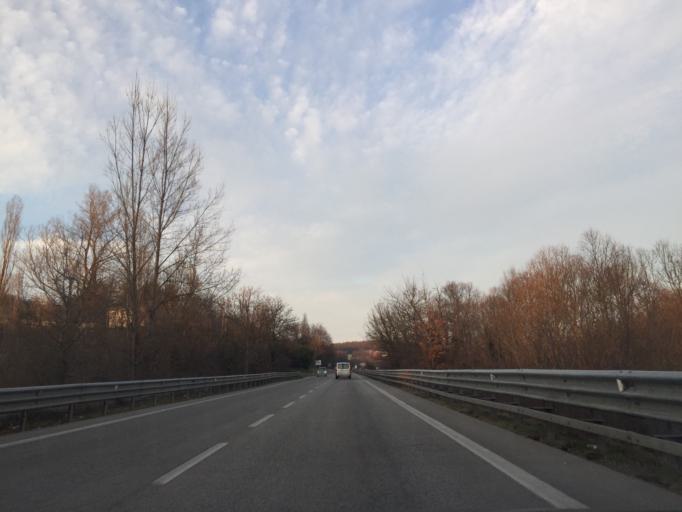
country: IT
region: Molise
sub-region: Provincia di Campobasso
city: Mimosa-Poggio Verde-Nuova Comunita
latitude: 41.5398
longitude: 14.6189
